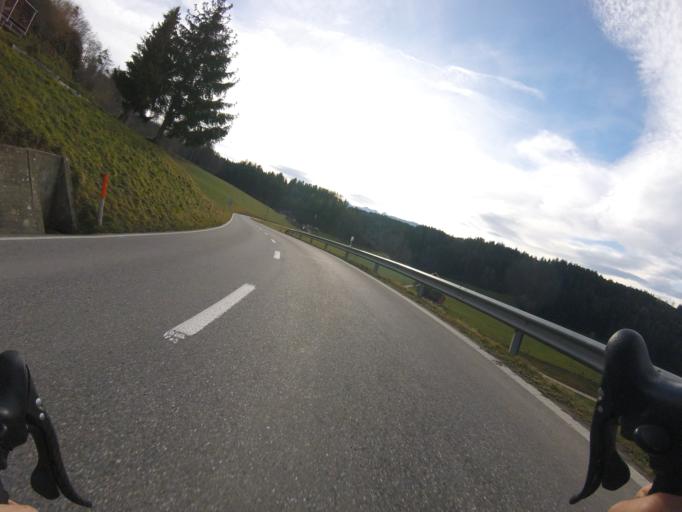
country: CH
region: Fribourg
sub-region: Sense District
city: Ueberstorf
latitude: 46.8505
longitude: 7.3207
